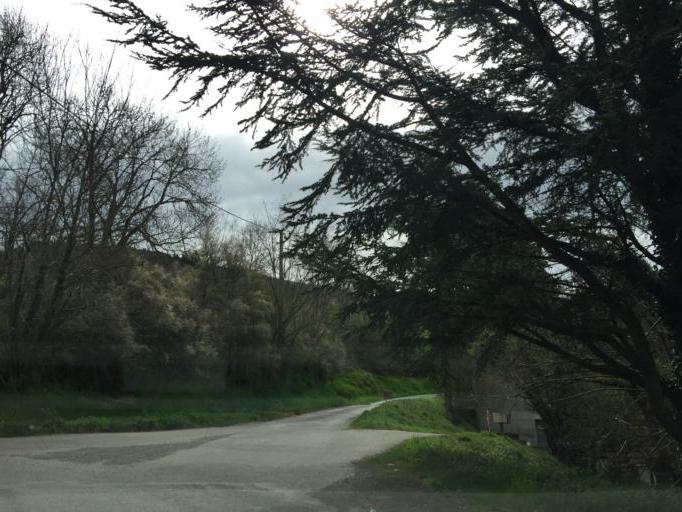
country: FR
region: Rhone-Alpes
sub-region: Departement de la Loire
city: Saint-Paul-en-Jarez
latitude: 45.4728
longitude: 4.5863
